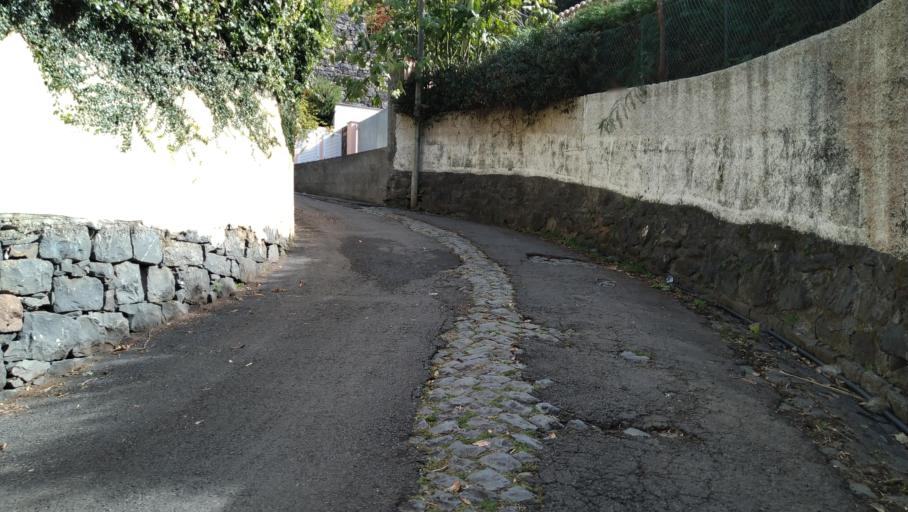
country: PT
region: Madeira
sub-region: Funchal
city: Nossa Senhora do Monte
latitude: 32.6601
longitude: -16.8773
